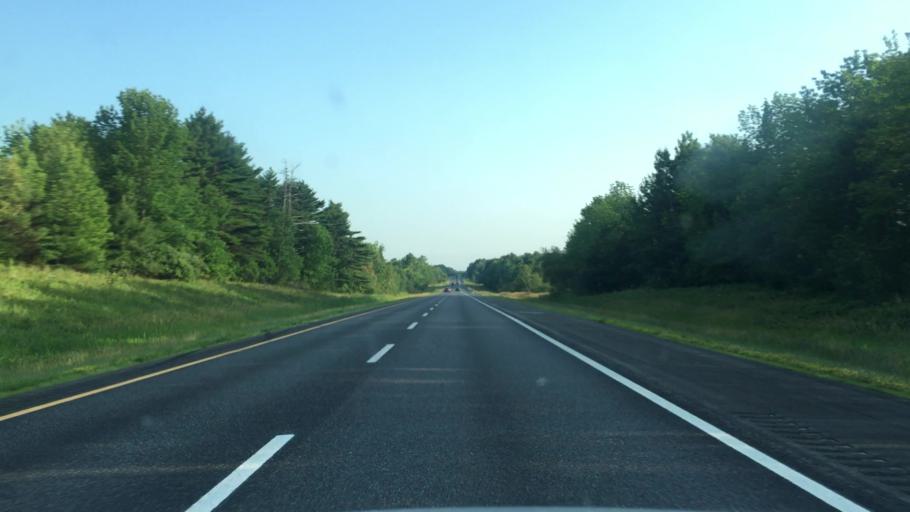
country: US
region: Maine
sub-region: Sagadahoc County
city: Richmond
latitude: 44.1423
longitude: -69.8426
